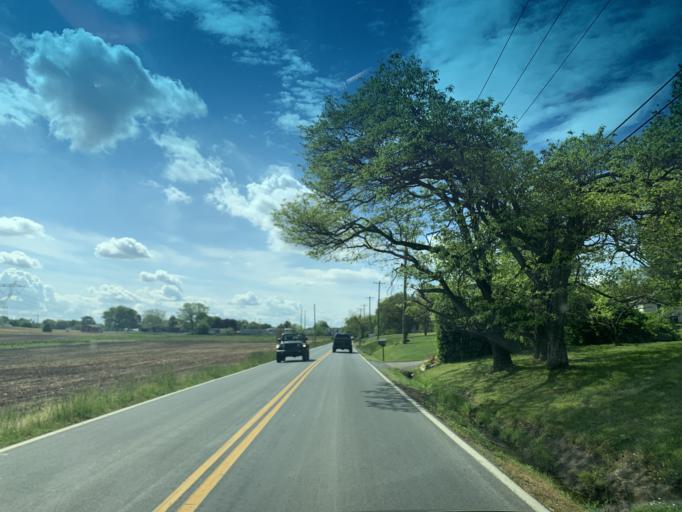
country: US
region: Maryland
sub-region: Cecil County
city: Rising Sun
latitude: 39.7139
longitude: -76.1549
